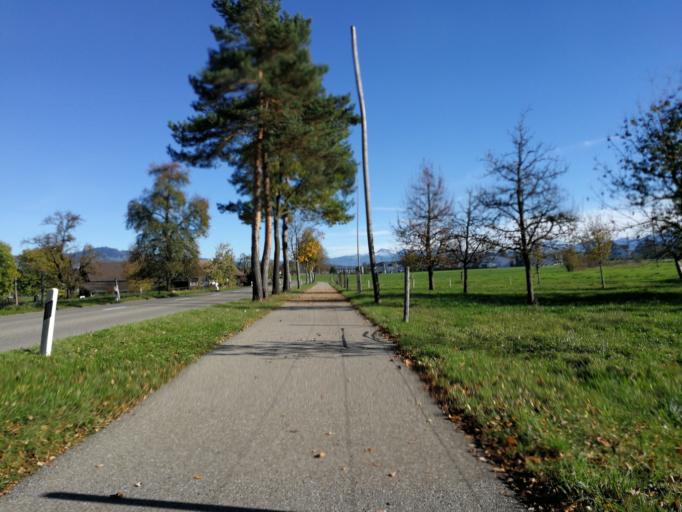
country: CH
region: Zurich
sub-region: Bezirk Hinwil
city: Binzikon
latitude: 47.2850
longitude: 8.7518
